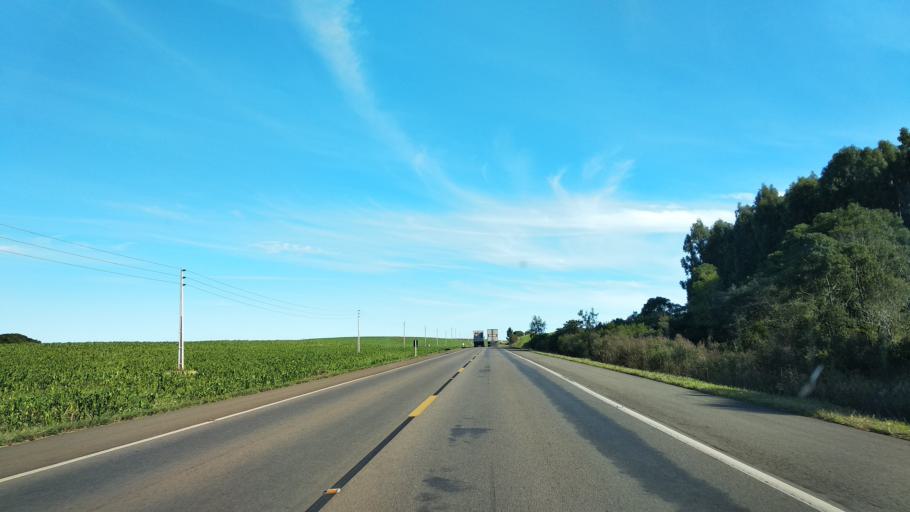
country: BR
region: Santa Catarina
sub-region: Celso Ramos
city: Celso Ramos
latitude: -27.5153
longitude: -51.3494
